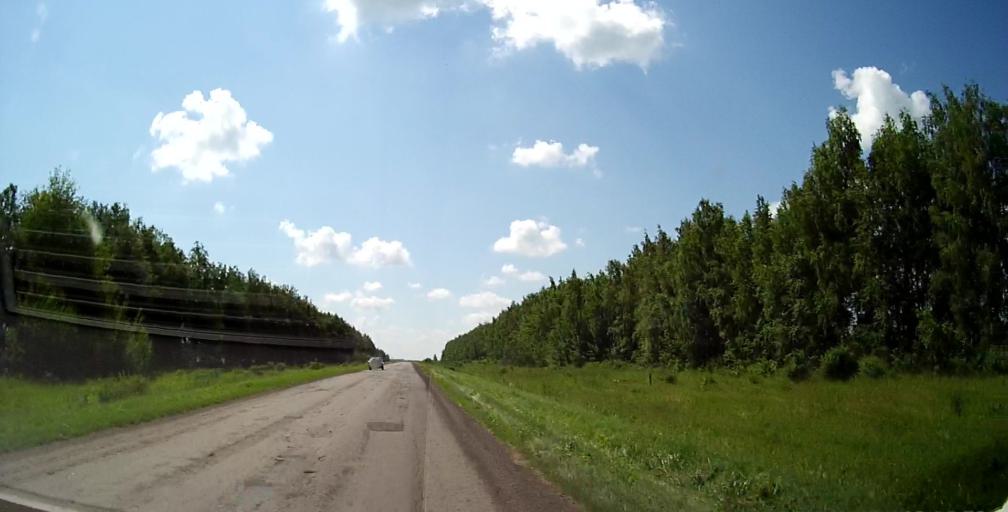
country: RU
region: Lipetsk
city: Chaplygin
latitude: 53.3642
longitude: 39.9185
